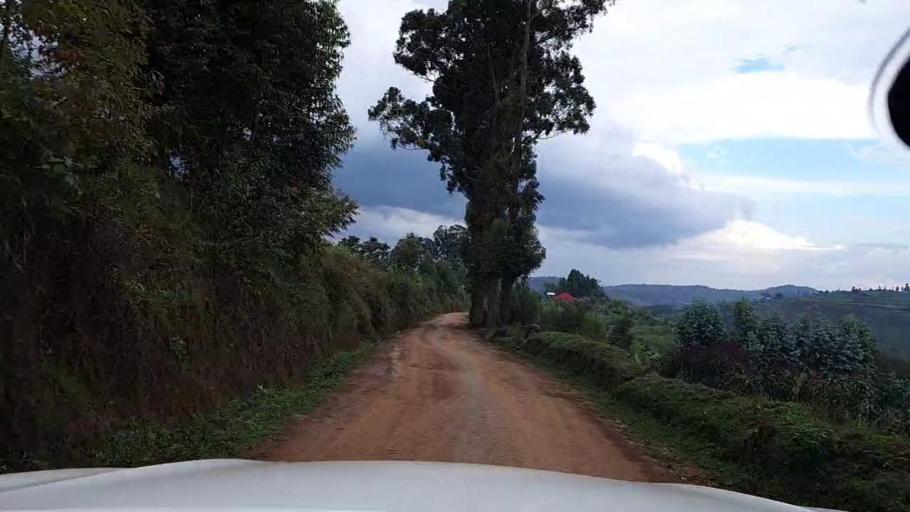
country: BI
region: Kayanza
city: Kayanza
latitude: -2.7951
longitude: 29.5138
